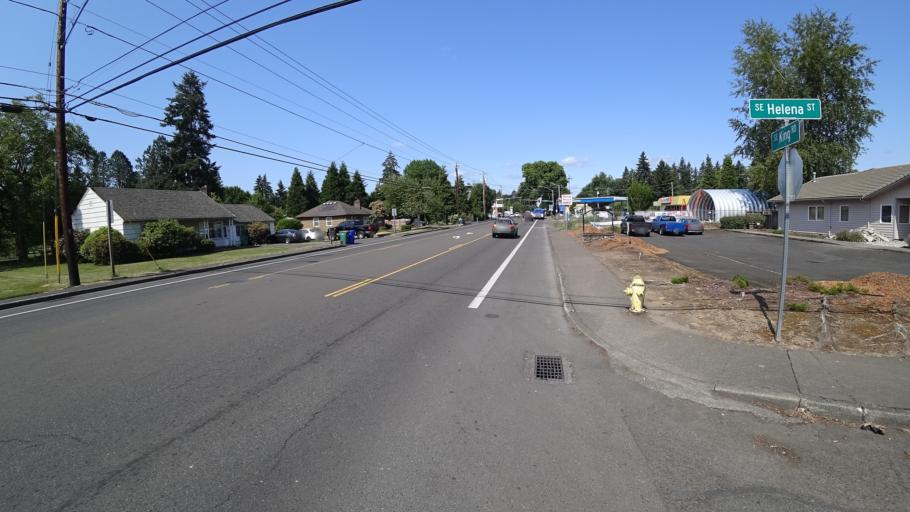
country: US
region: Oregon
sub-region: Clackamas County
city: Oatfield
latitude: 45.4480
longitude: -122.5973
